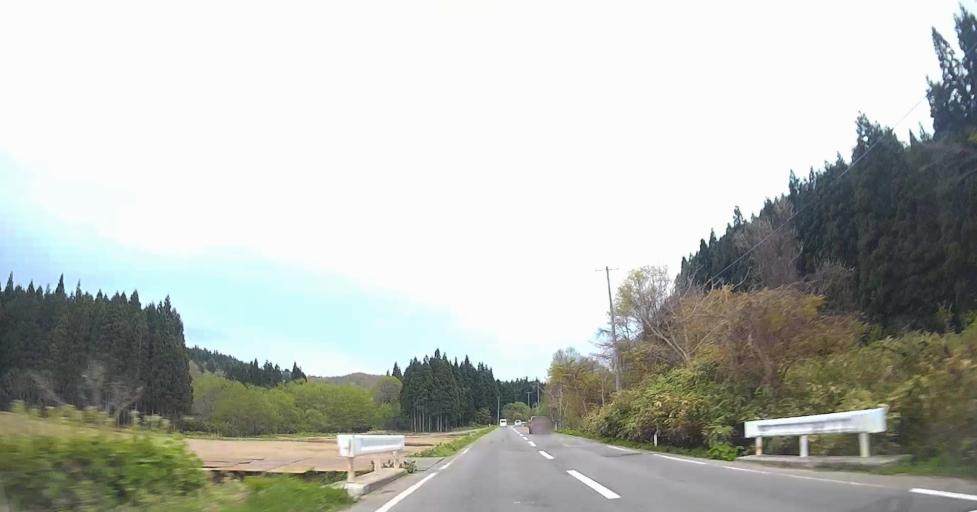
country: JP
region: Aomori
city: Goshogawara
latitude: 41.1224
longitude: 140.5219
